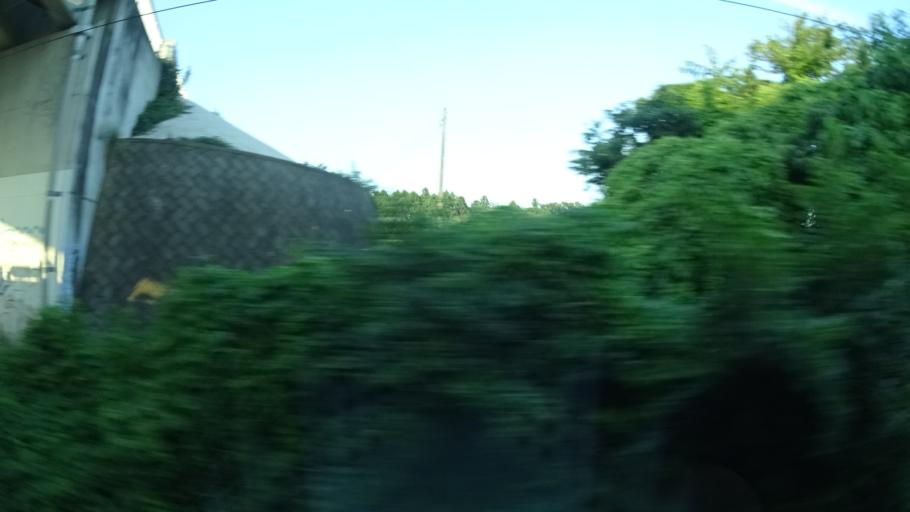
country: JP
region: Ibaraki
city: Tomobe
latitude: 36.2847
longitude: 140.2776
